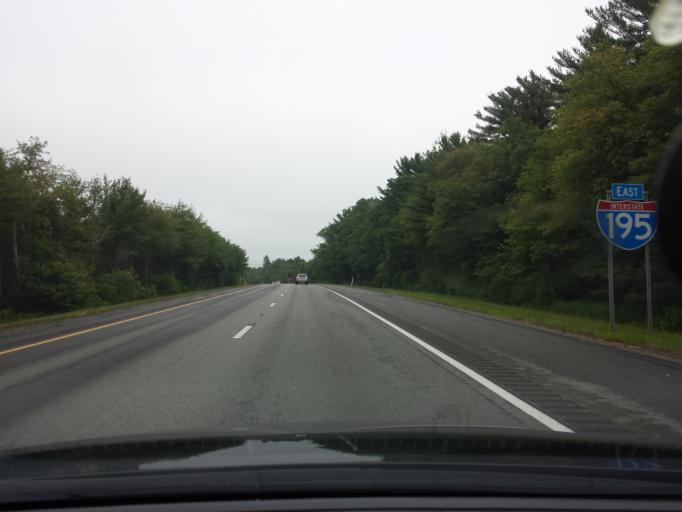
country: US
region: Massachusetts
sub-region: Plymouth County
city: Mattapoisett
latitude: 41.6684
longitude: -70.8316
